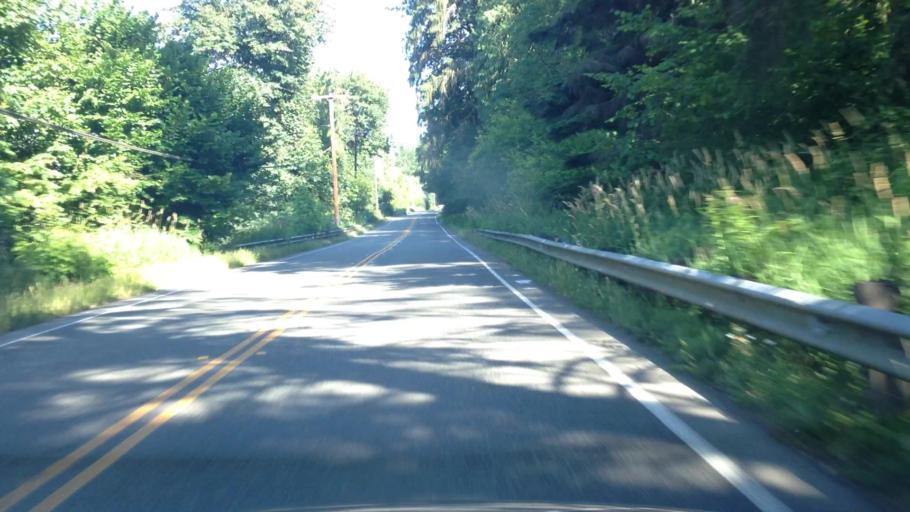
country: US
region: Washington
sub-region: King County
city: Duvall
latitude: 47.7457
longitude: -121.9553
